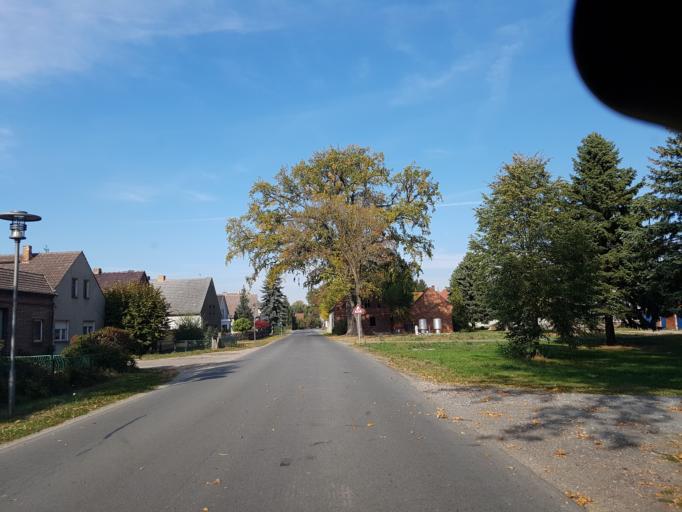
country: DE
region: Brandenburg
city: Doberlug-Kirchhain
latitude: 51.6725
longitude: 13.5106
